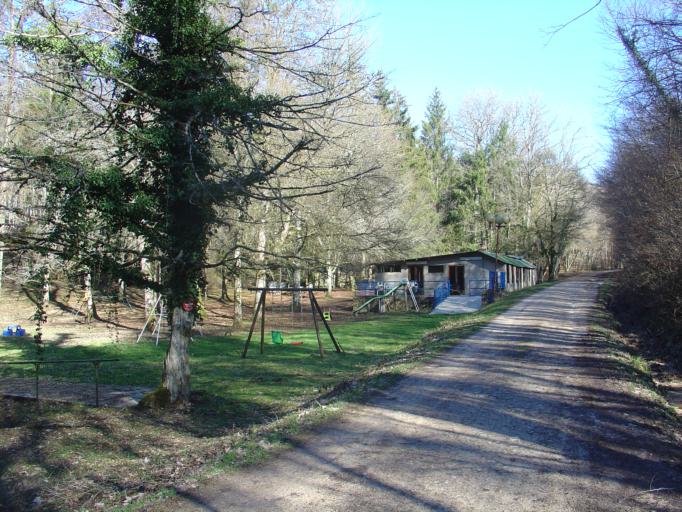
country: FR
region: Lorraine
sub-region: Departement de Meurthe-et-Moselle
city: Blenod-les-Toul
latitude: 48.5819
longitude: 5.8030
